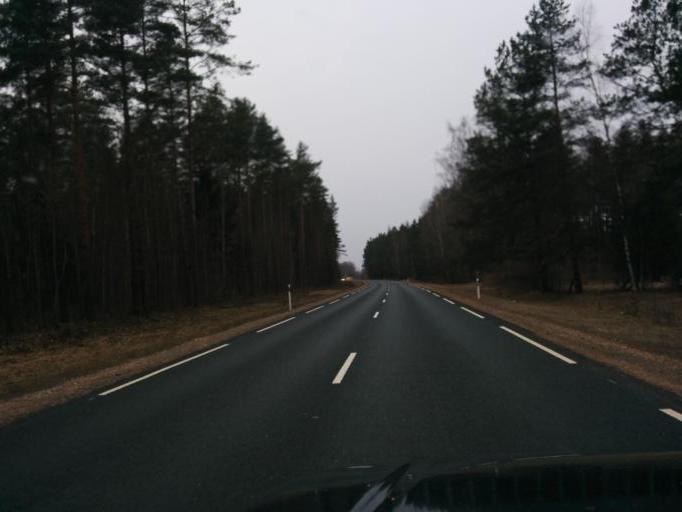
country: LV
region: Ogre
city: Ogre
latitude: 56.8036
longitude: 24.5756
